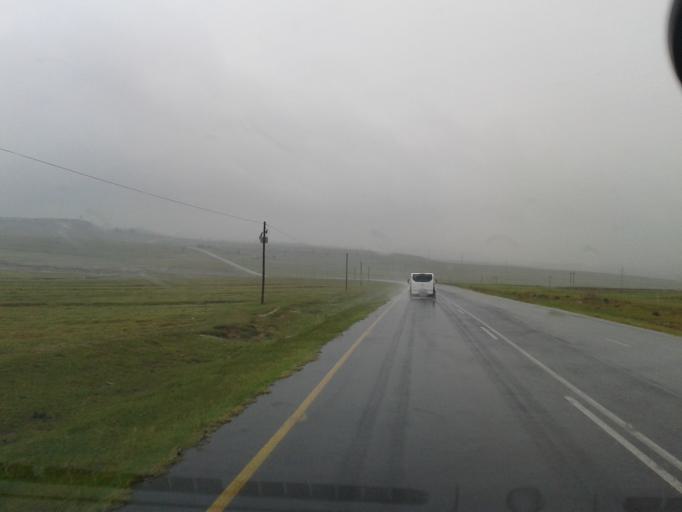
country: LS
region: Mafeteng
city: Mafeteng
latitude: -29.6519
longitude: 27.4592
